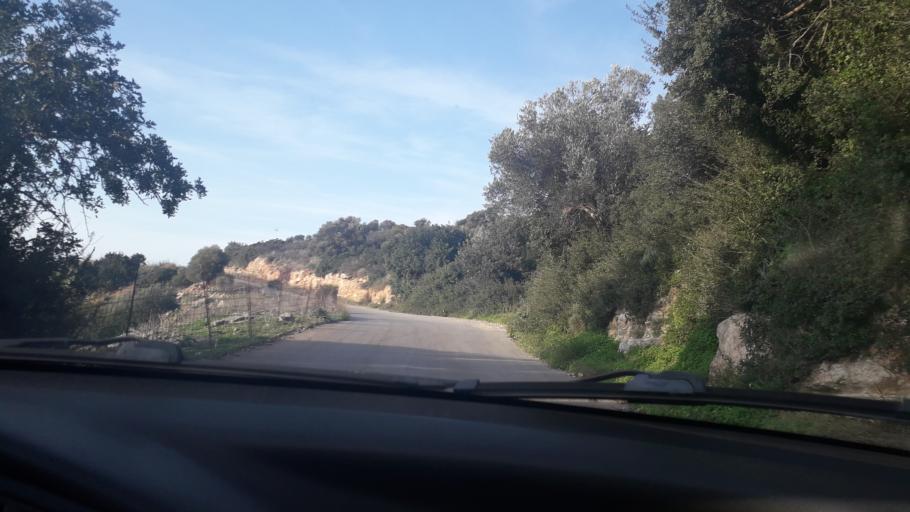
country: GR
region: Crete
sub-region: Nomos Rethymnis
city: Panormos
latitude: 35.3830
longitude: 24.6238
